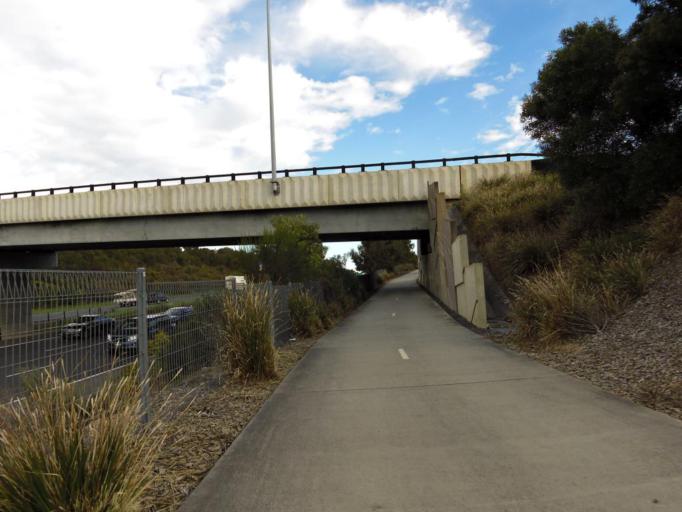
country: AU
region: Victoria
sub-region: Knox
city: Wantirna South
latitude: -37.8887
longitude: 145.2145
